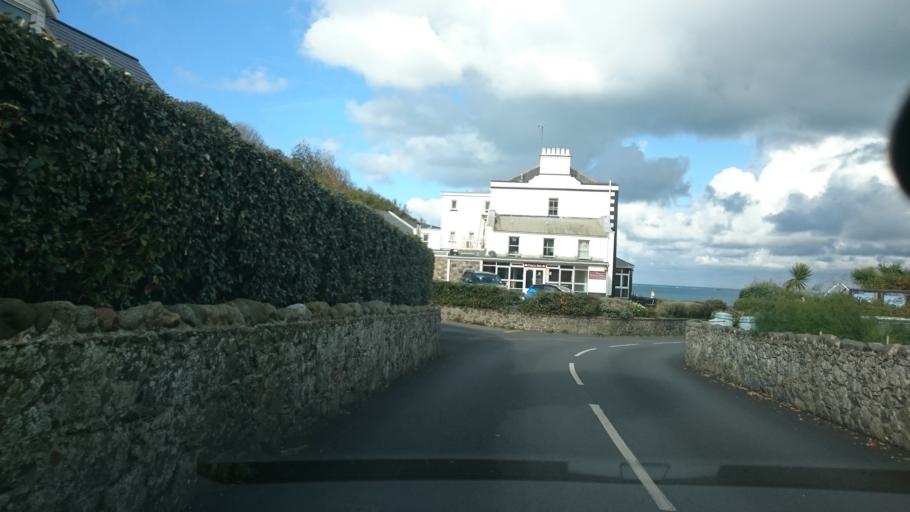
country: GG
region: St Peter Port
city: Saint Peter Port
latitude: 49.4335
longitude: -2.6595
